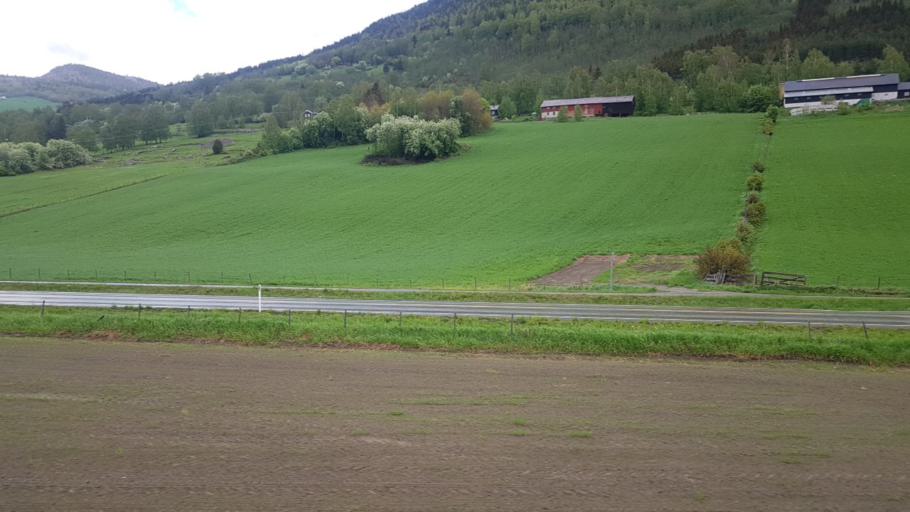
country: NO
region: Oppland
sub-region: Nord-Fron
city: Vinstra
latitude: 61.6639
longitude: 9.6836
